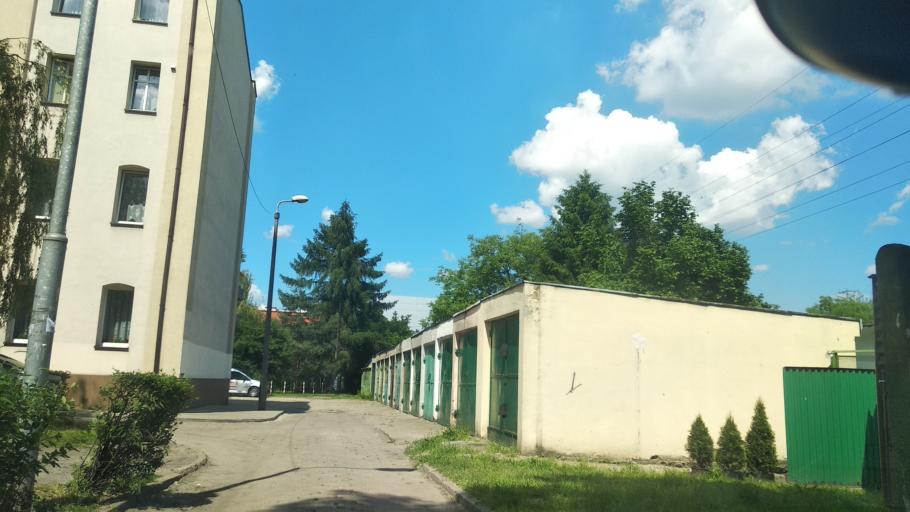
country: PL
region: Silesian Voivodeship
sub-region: Katowice
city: Katowice
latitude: 50.2610
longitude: 19.0052
